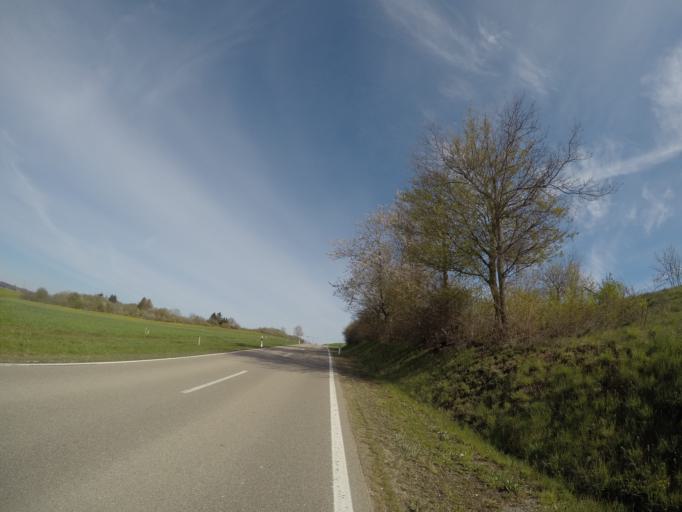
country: DE
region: Baden-Wuerttemberg
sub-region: Tuebingen Region
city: Laichingen
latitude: 48.4993
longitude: 9.6777
